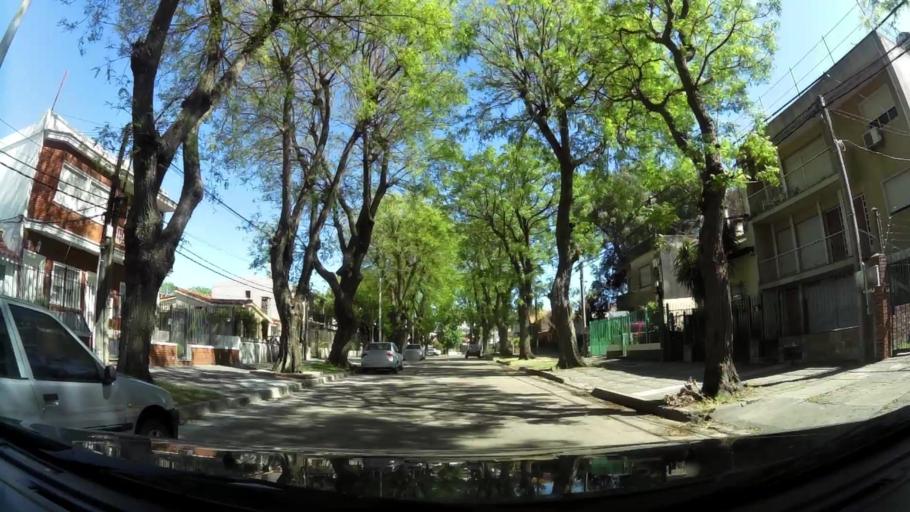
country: UY
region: Canelones
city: Paso de Carrasco
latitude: -34.8902
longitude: -56.1123
